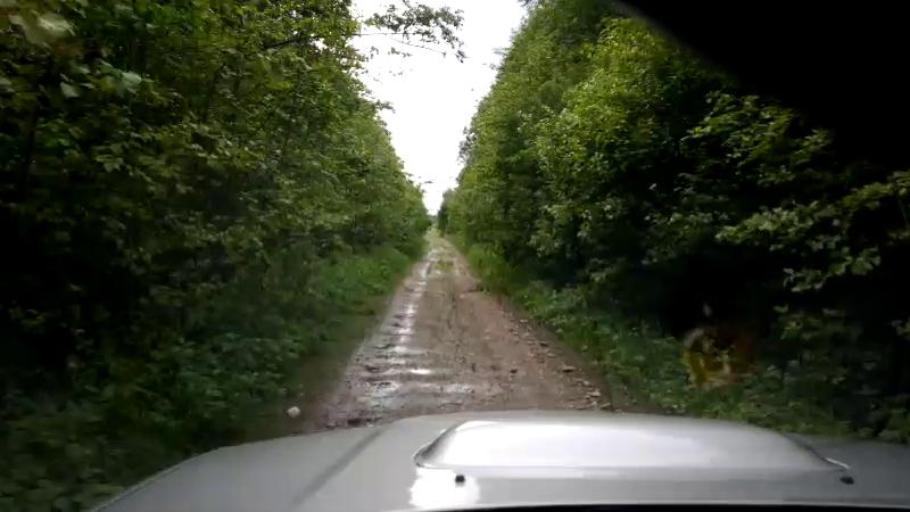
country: EE
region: Paernumaa
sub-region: Halinga vald
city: Parnu-Jaagupi
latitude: 58.5654
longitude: 24.5624
